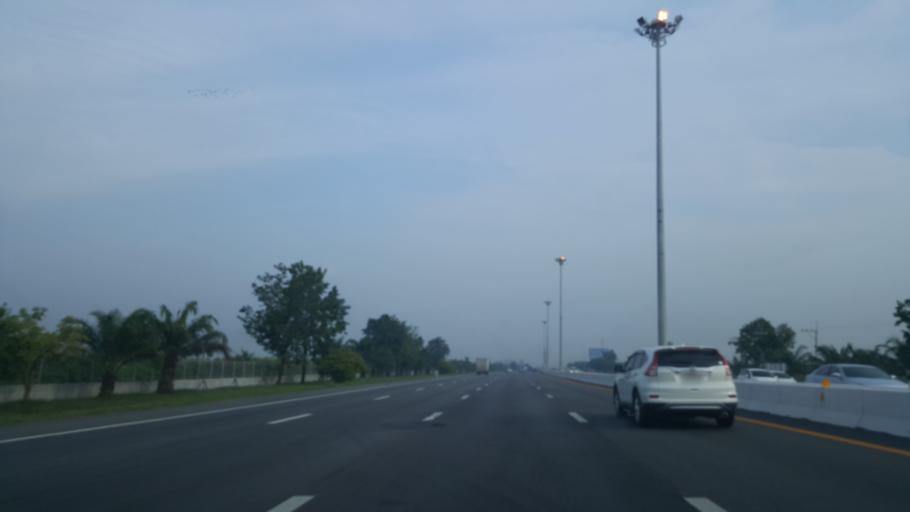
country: TH
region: Chon Buri
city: Phan Thong
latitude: 13.4702
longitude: 101.0459
